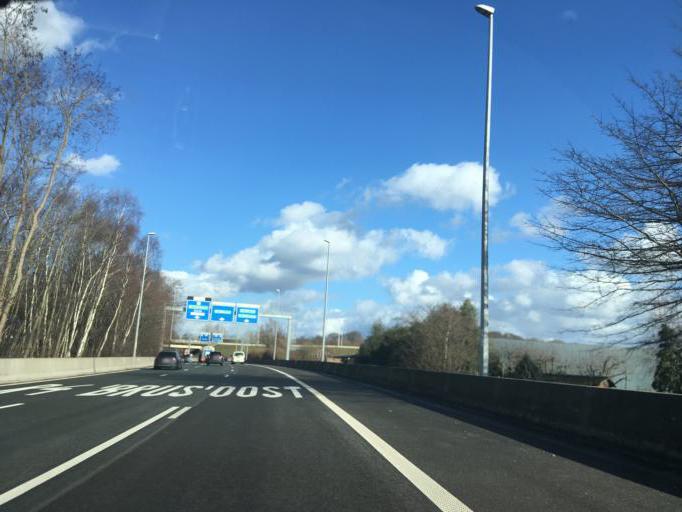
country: BE
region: Flanders
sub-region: Provincie Oost-Vlaanderen
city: Merelbeke
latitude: 51.0041
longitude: 3.7652
